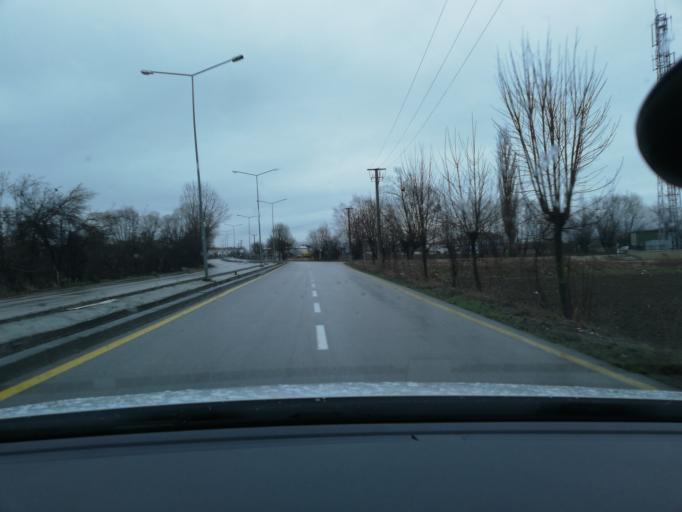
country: TR
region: Bolu
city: Bolu
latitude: 40.7283
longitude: 31.6291
